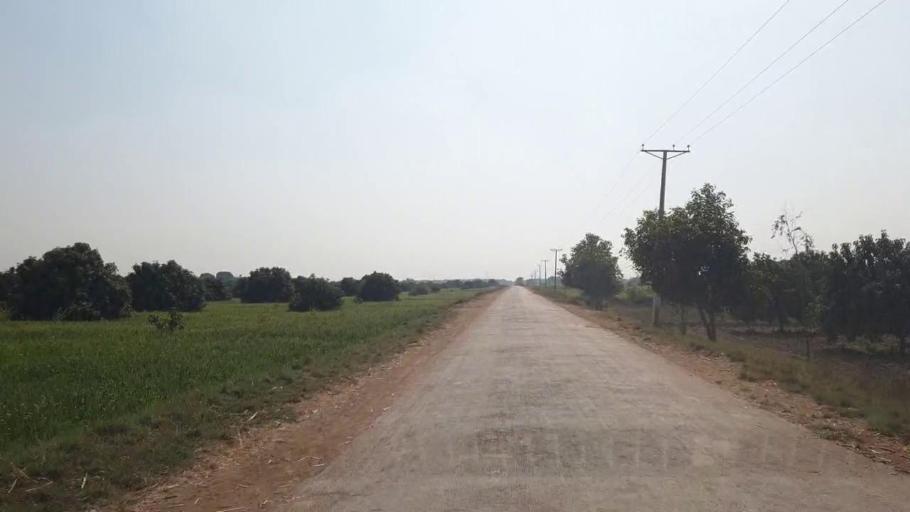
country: PK
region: Sindh
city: Chambar
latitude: 25.4001
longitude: 68.8958
